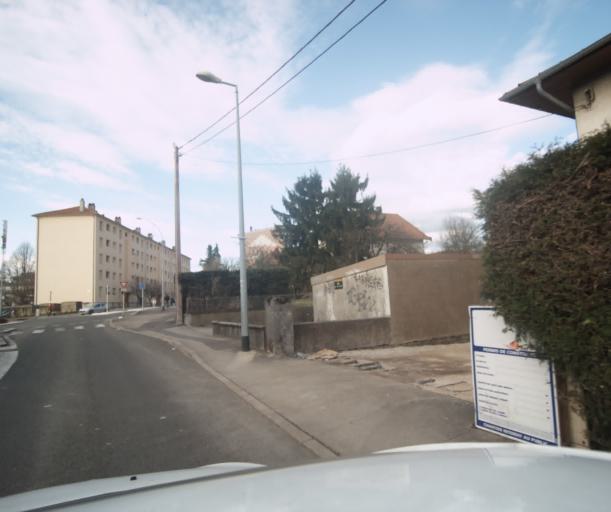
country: FR
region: Franche-Comte
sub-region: Departement du Doubs
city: Besancon
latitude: 47.2602
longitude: 6.0277
